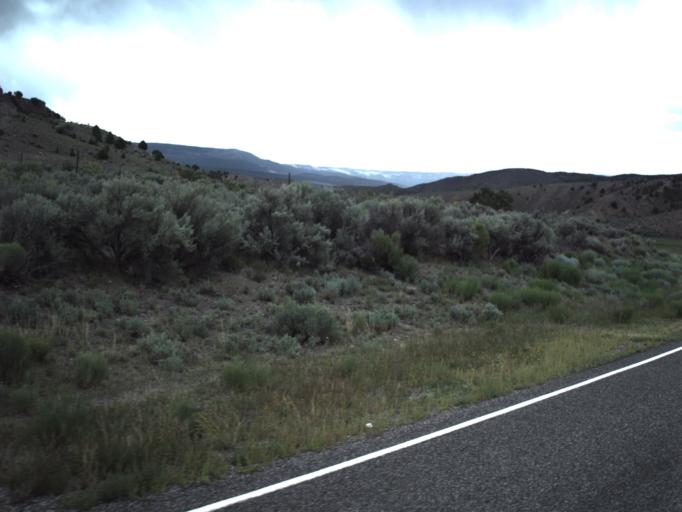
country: US
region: Utah
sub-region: Piute County
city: Junction
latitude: 38.1794
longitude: -112.0788
